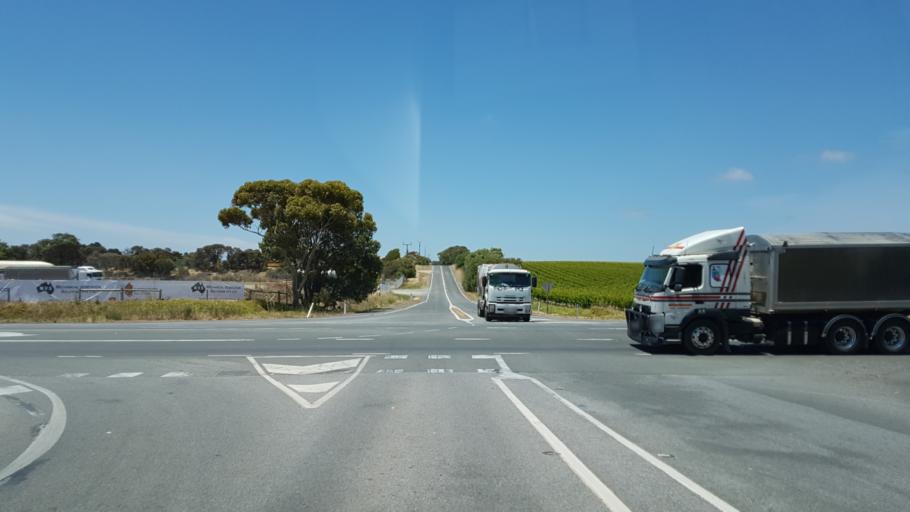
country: AU
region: South Australia
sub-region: Onkaparinga
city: Moana
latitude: -35.2325
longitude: 138.4931
